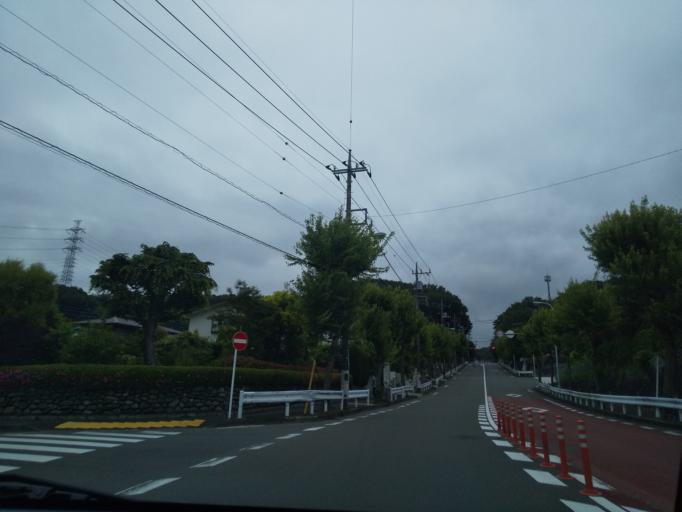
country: JP
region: Tokyo
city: Hino
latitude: 35.6458
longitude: 139.3901
